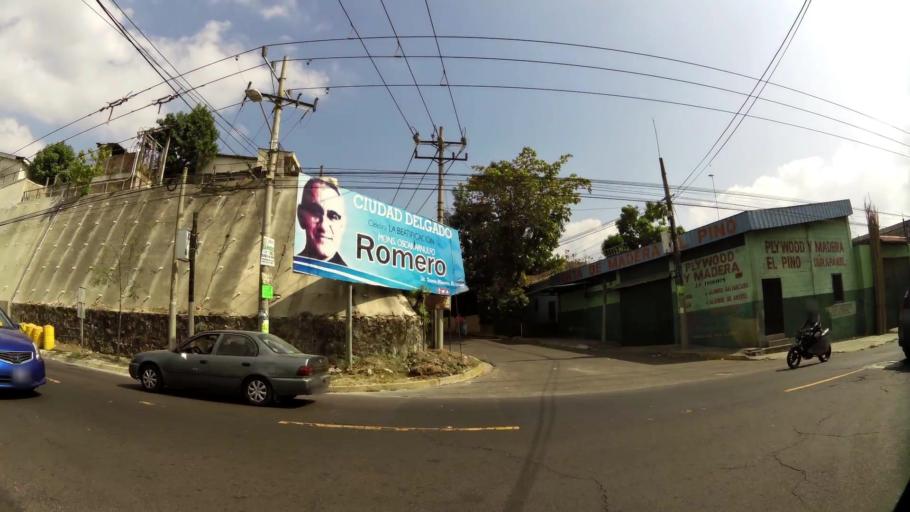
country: SV
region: San Salvador
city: Delgado
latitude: 13.7128
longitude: -89.1714
